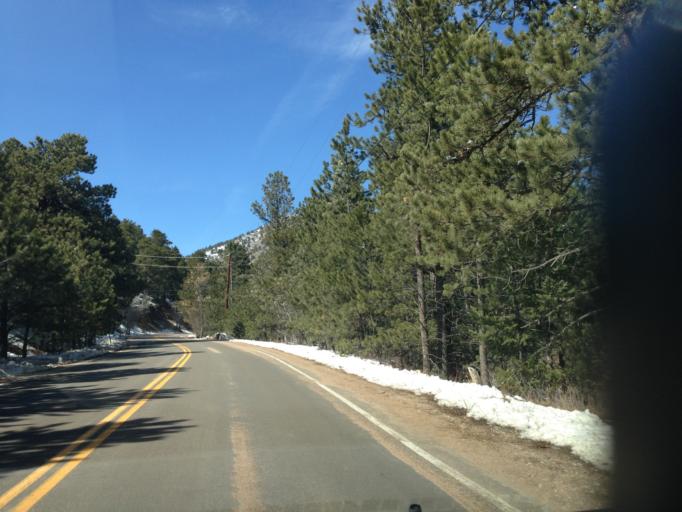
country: US
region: Colorado
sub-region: Boulder County
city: Lyons
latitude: 40.1231
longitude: -105.3973
